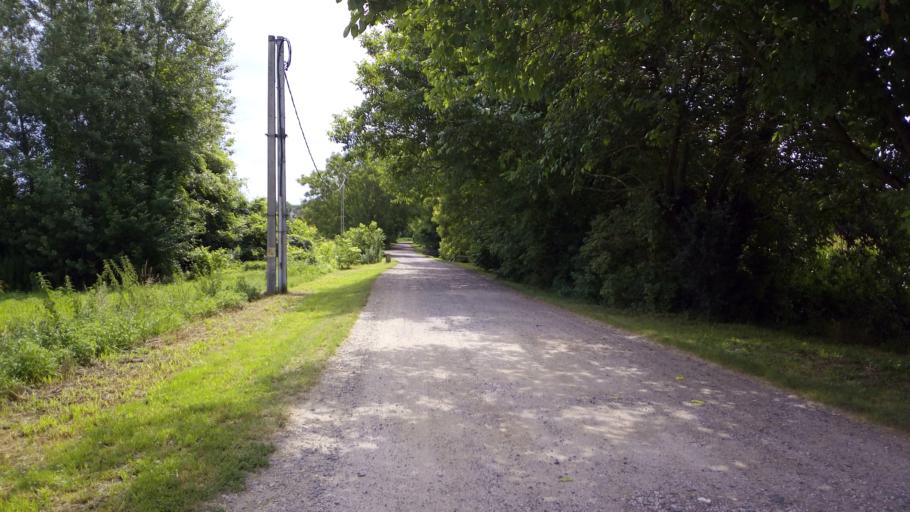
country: HU
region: Somogy
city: Balatonbereny
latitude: 46.7063
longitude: 17.3282
